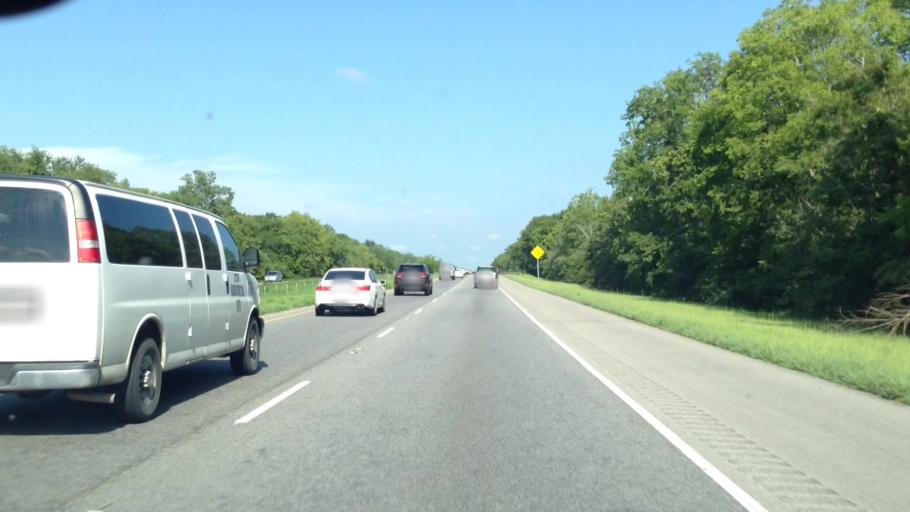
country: US
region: Louisiana
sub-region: Saint John the Baptist Parish
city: Reserve
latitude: 30.1141
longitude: -90.5773
